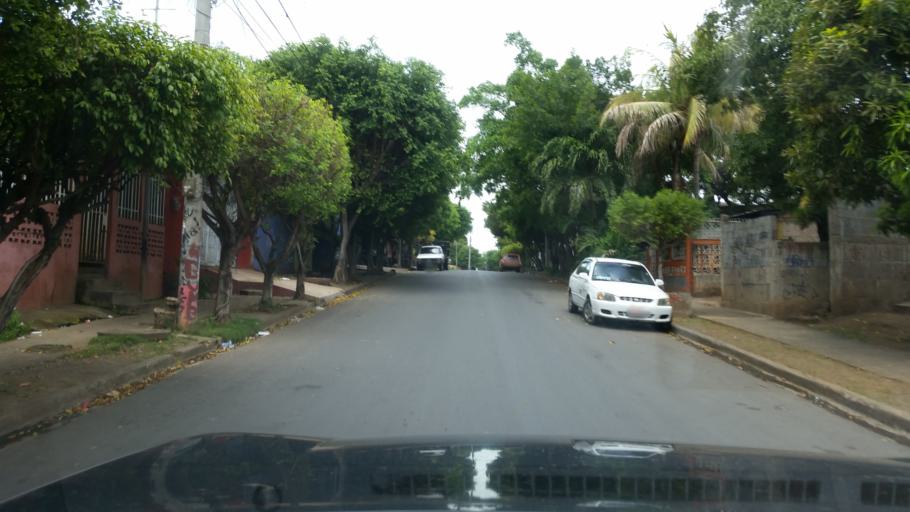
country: NI
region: Managua
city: Managua
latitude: 12.1363
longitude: -86.2196
